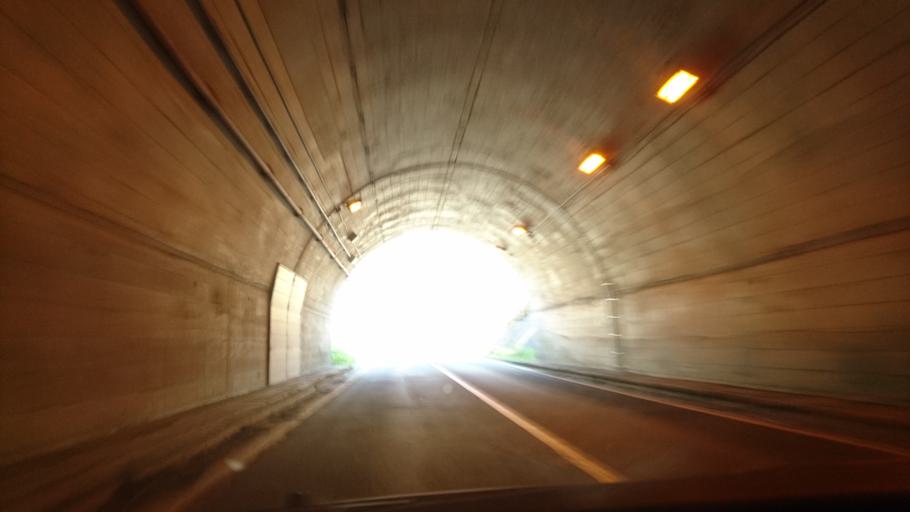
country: JP
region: Iwate
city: Kitakami
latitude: 39.3046
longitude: 140.8927
